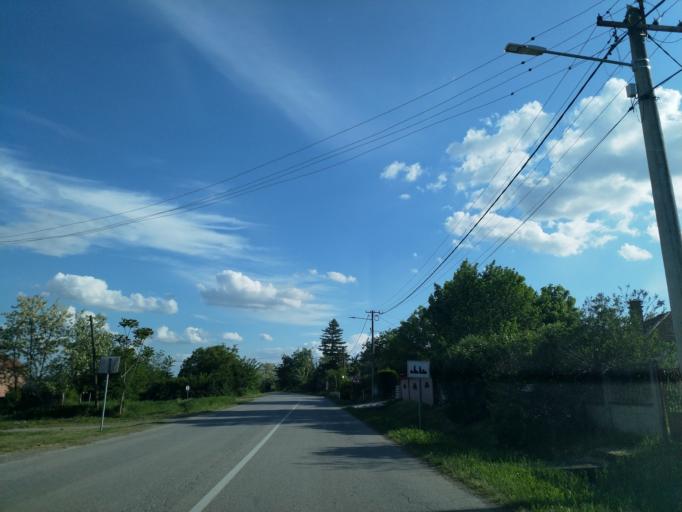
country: RS
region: Central Serbia
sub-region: Sumadijski Okrug
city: Lapovo
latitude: 44.2012
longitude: 21.0888
